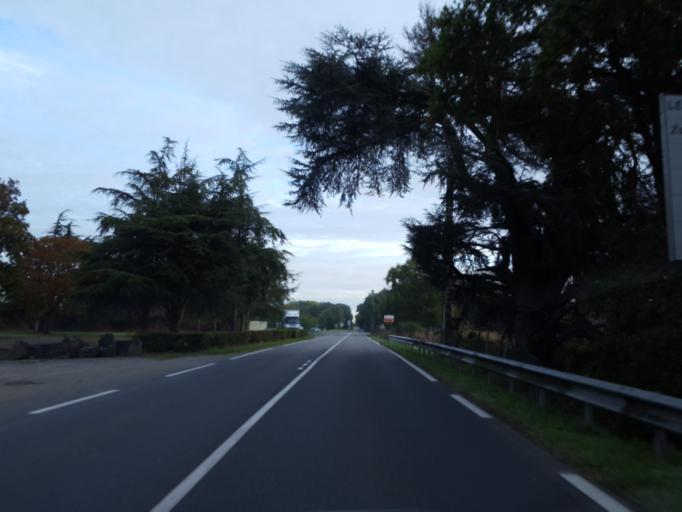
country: FR
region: Pays de la Loire
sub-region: Departement de la Loire-Atlantique
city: Haute-Goulaine
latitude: 47.2143
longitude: -1.4380
